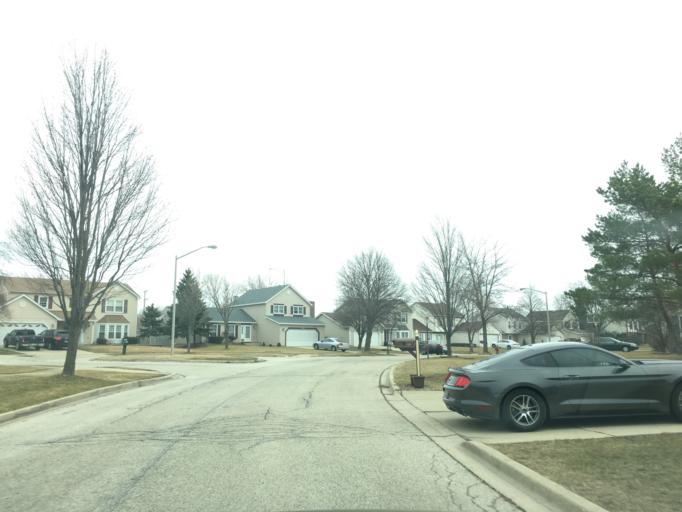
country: US
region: Illinois
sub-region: Cook County
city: Schaumburg
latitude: 42.0469
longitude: -88.1121
